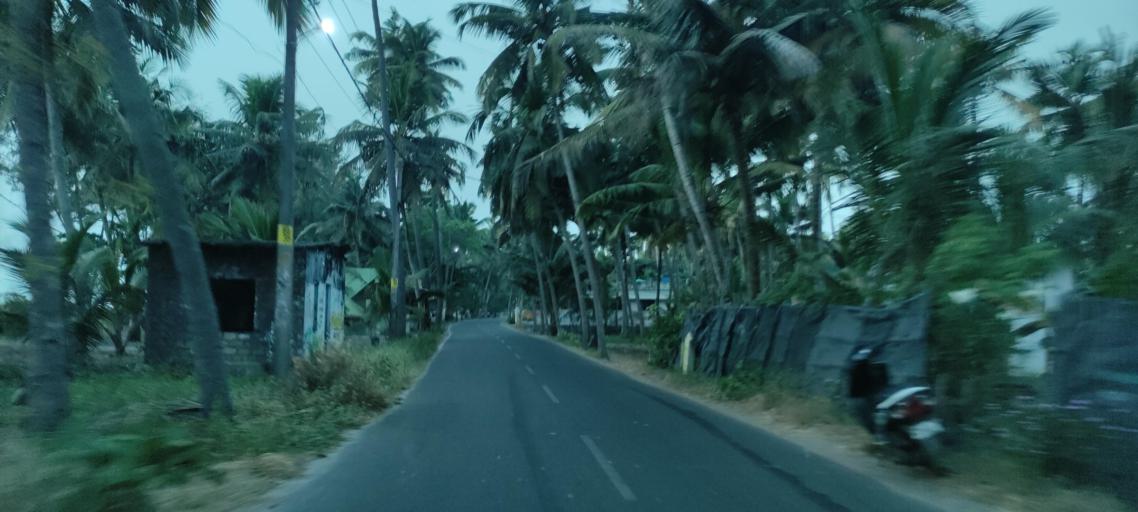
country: IN
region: Kerala
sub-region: Alappuzha
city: Kayankulam
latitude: 9.1284
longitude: 76.4666
